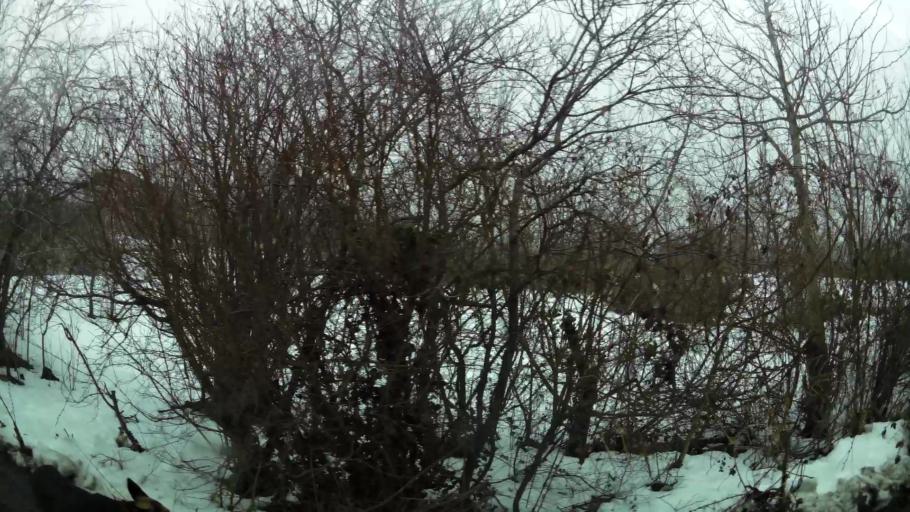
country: RS
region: Central Serbia
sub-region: Belgrade
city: Zvezdara
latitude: 44.7572
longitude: 20.5217
